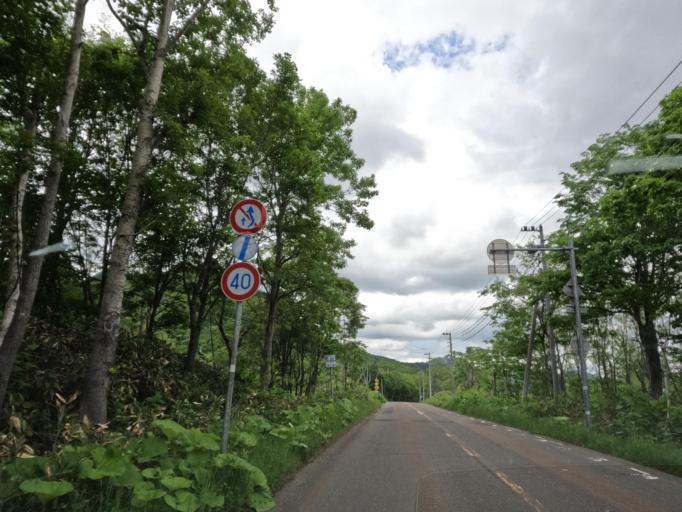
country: JP
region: Hokkaido
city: Takikawa
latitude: 43.5625
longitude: 141.7004
